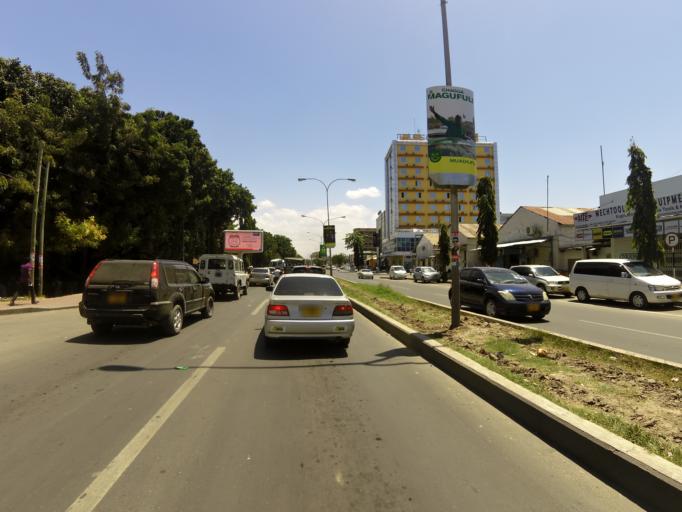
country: TZ
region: Dar es Salaam
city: Dar es Salaam
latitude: -6.8257
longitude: 39.2795
